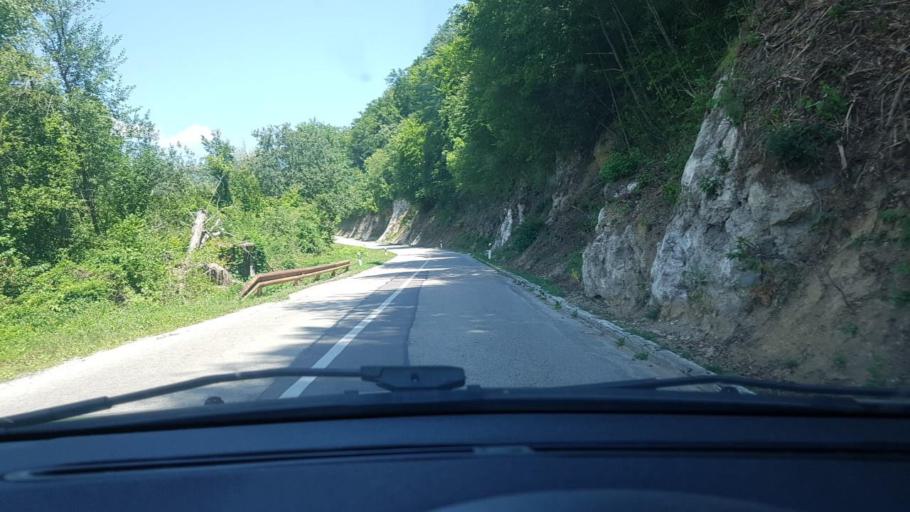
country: BA
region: Federation of Bosnia and Herzegovina
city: Orasac
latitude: 44.5875
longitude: 16.0817
